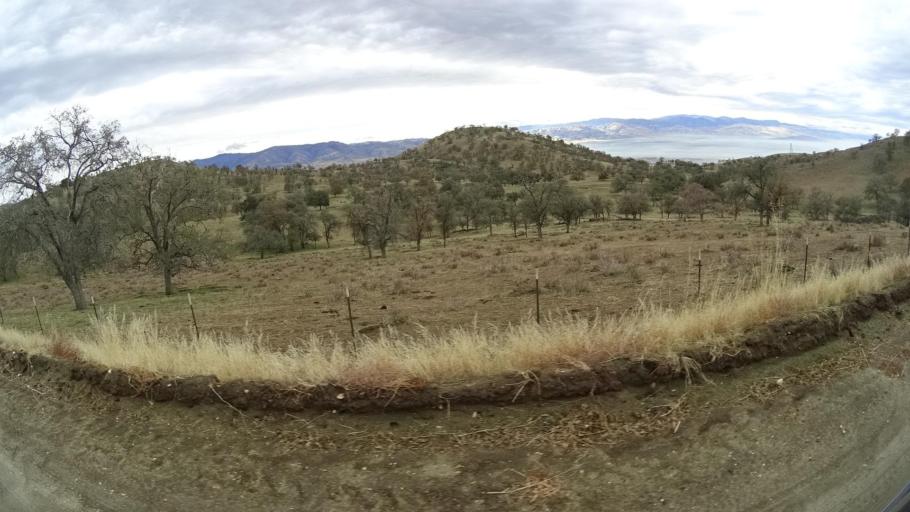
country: US
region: California
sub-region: Kern County
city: Stallion Springs
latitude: 35.1214
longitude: -118.7185
